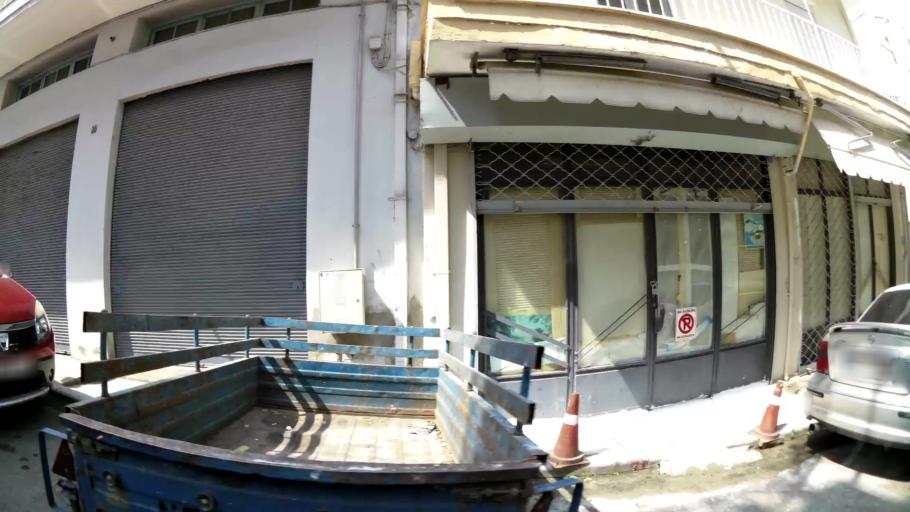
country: GR
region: Central Macedonia
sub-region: Nomos Thessalonikis
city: Sykies
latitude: 40.6495
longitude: 22.9453
